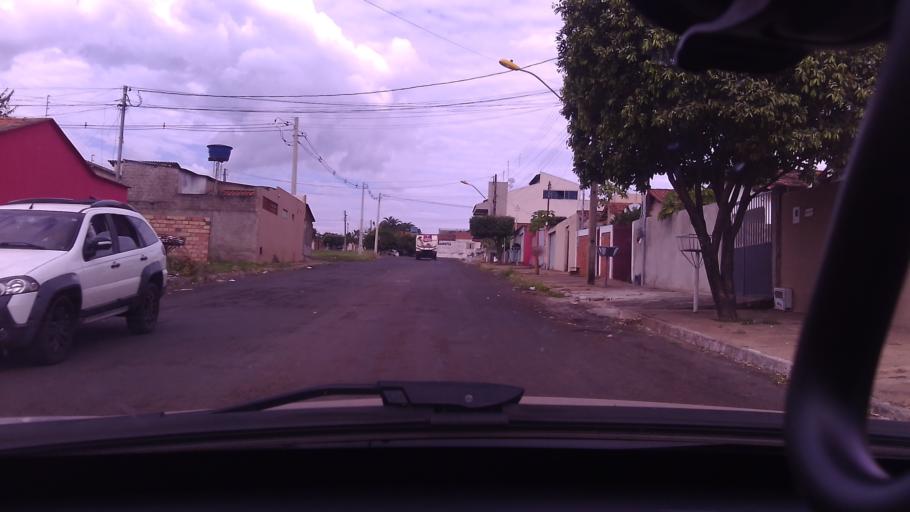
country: BR
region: Goias
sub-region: Mineiros
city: Mineiros
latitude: -17.5704
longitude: -52.5390
